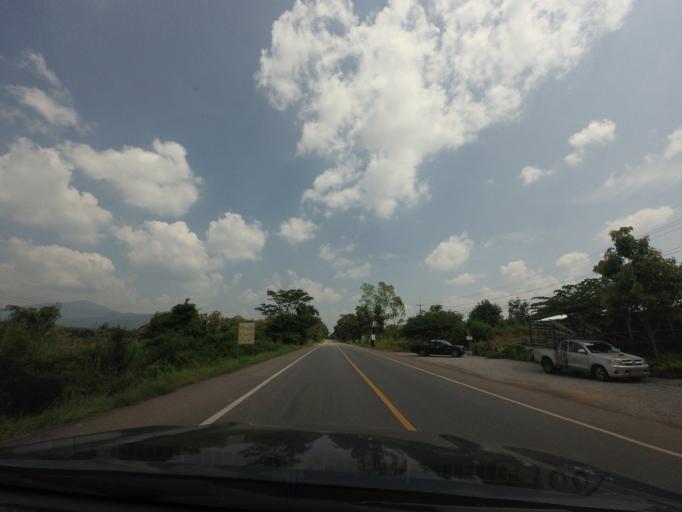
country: TH
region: Phitsanulok
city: Chat Trakan
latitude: 17.3086
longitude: 100.4792
